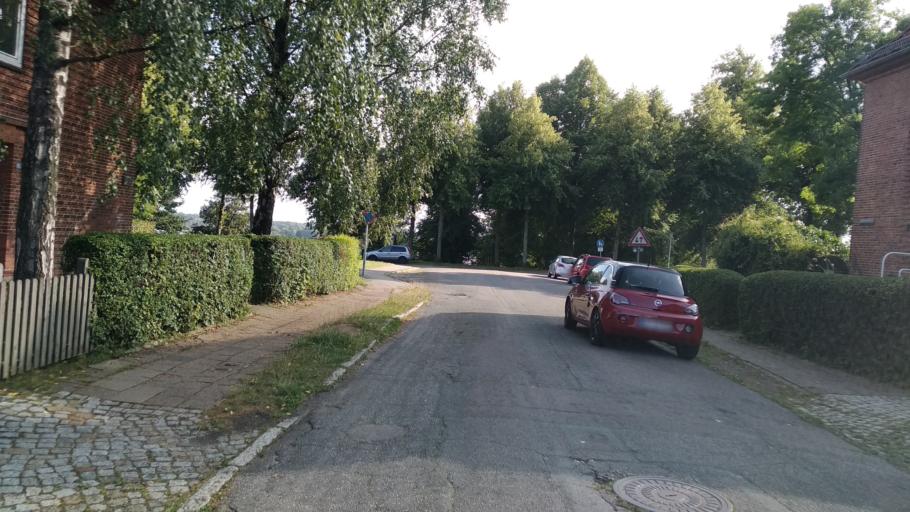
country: DE
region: Schleswig-Holstein
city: Schleswig
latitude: 54.5164
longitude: 9.5536
